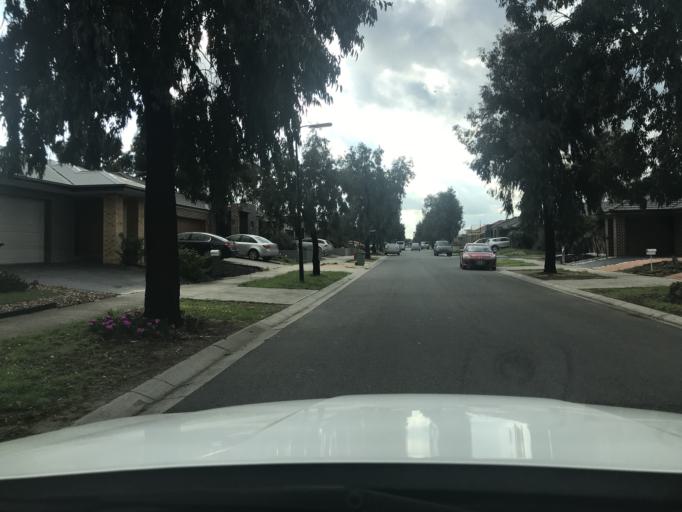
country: AU
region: Victoria
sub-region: Hume
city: Craigieburn
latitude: -37.5813
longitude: 144.9080
